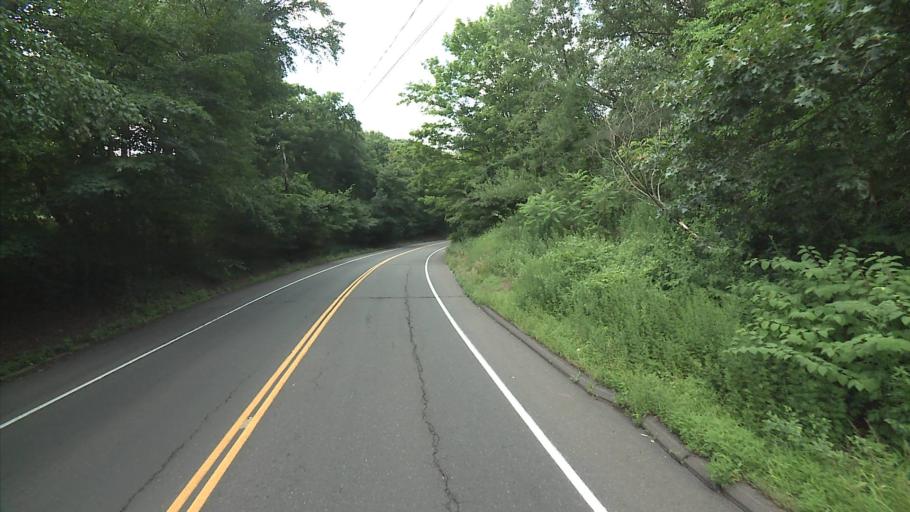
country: US
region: Connecticut
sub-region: New Haven County
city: North Haven
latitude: 41.3806
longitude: -72.8048
